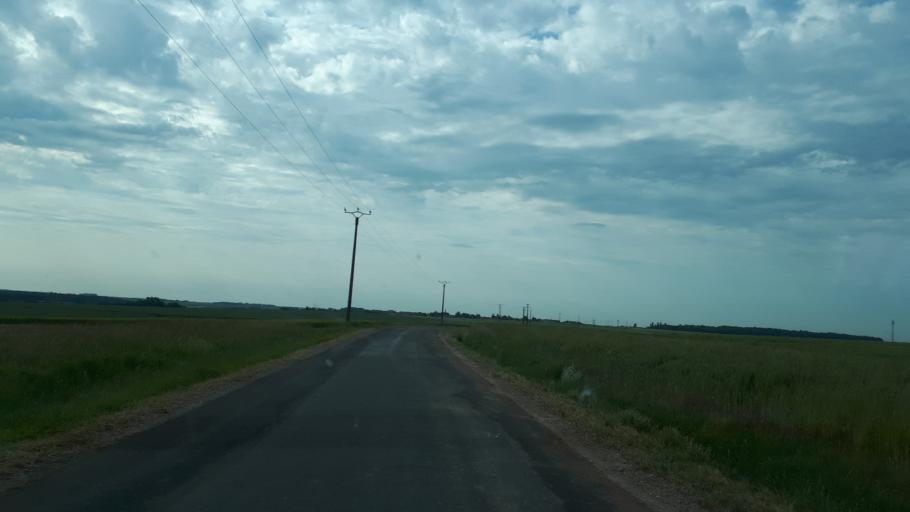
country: FR
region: Centre
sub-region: Departement du Loir-et-Cher
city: Saint-Amand-Longpre
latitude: 47.7371
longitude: 0.9974
